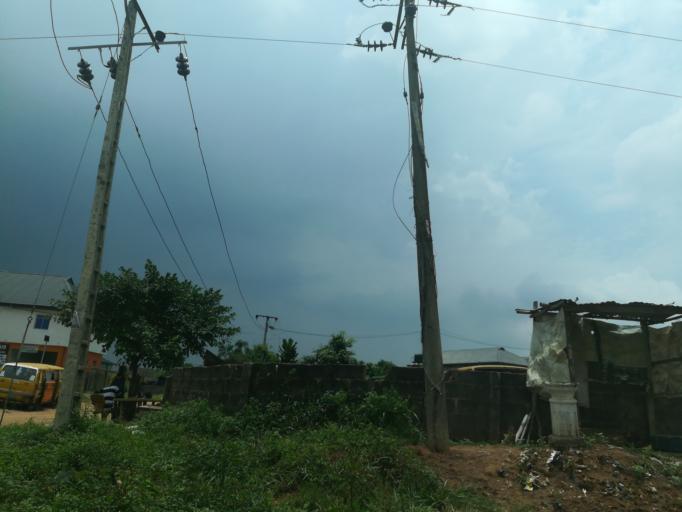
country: NG
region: Lagos
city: Ikorodu
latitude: 6.6123
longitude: 3.5790
